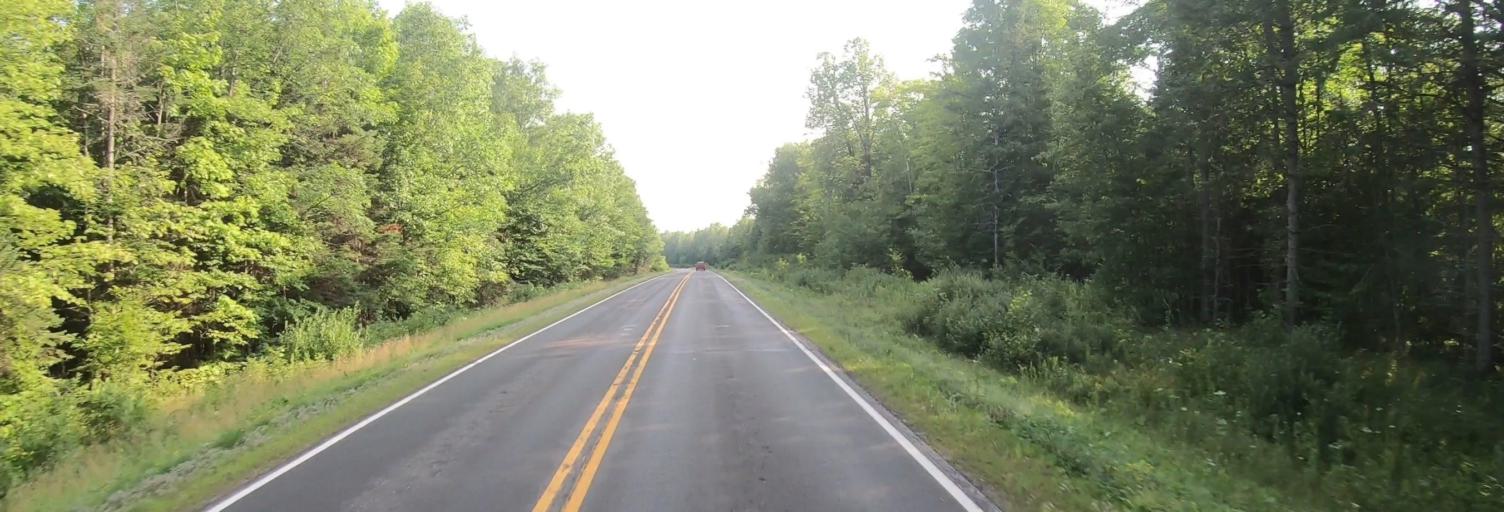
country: US
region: Wisconsin
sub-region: Ashland County
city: Ashland
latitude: 46.2443
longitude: -90.8331
